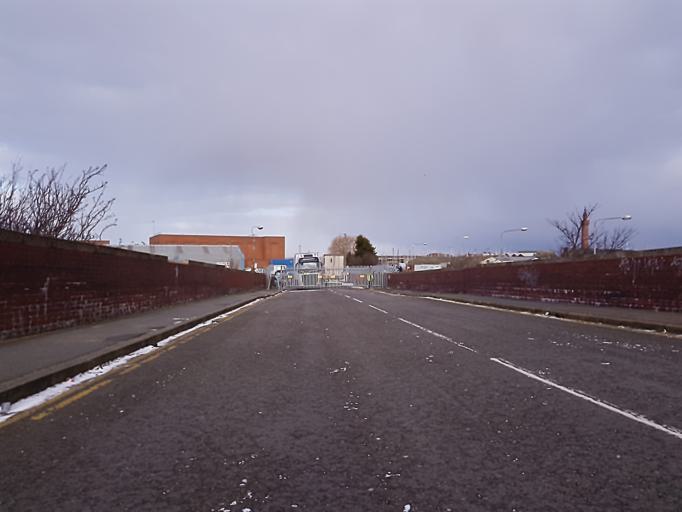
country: GB
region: England
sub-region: North East Lincolnshire
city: Grimsby
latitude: 53.5750
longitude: -0.0633
